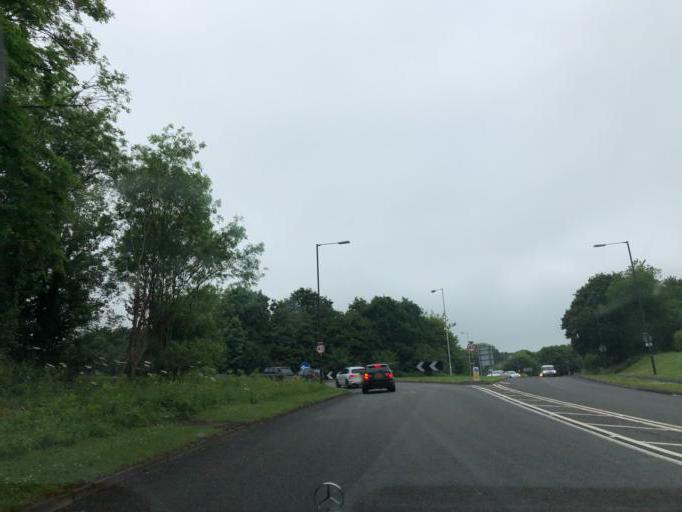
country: GB
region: England
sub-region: Warwickshire
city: Warwick
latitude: 52.2893
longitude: -1.6083
